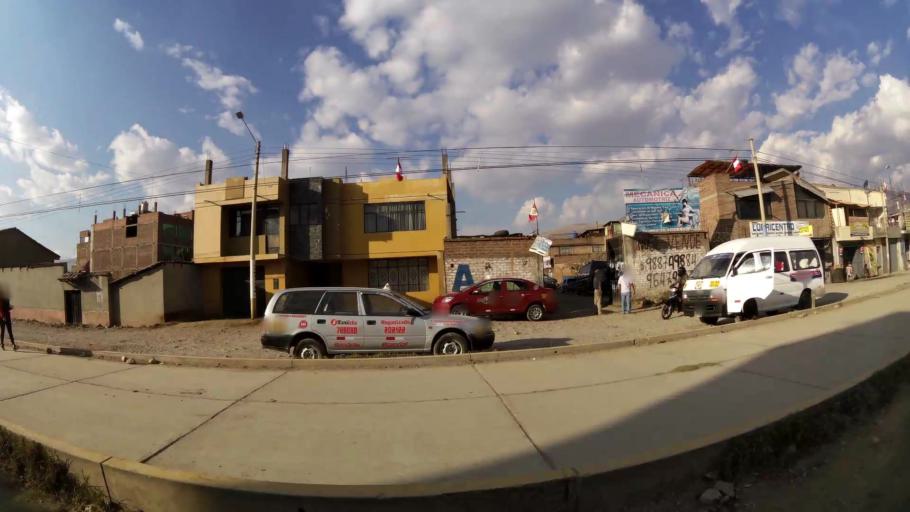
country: PE
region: Junin
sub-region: Provincia de Huancayo
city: El Tambo
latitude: -12.0519
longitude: -75.2177
